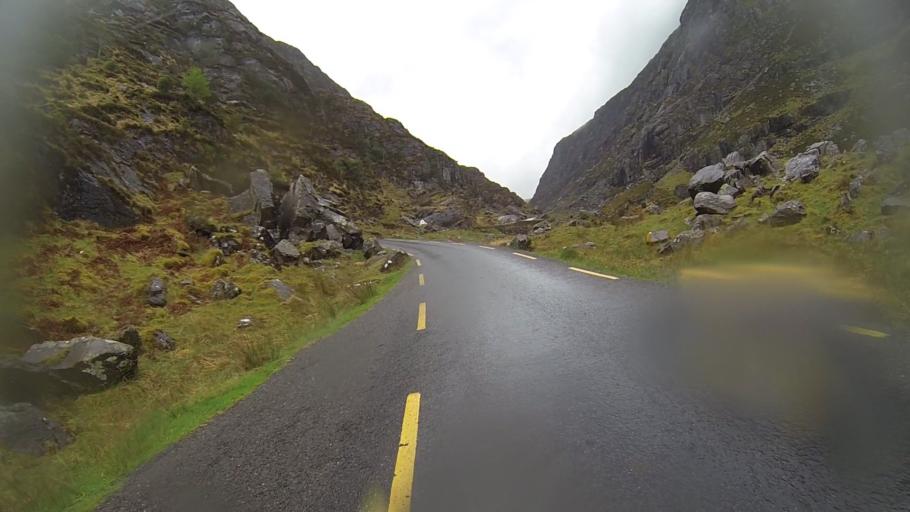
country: IE
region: Munster
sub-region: Ciarrai
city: Cill Airne
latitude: 52.0103
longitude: -9.6389
